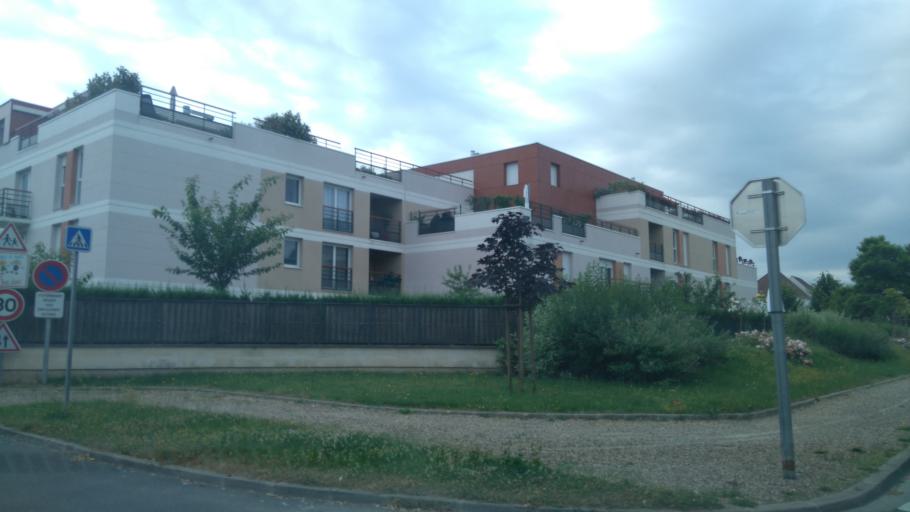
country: FR
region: Picardie
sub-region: Departement de l'Oise
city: Saint-Maximin
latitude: 49.2228
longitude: 2.4553
